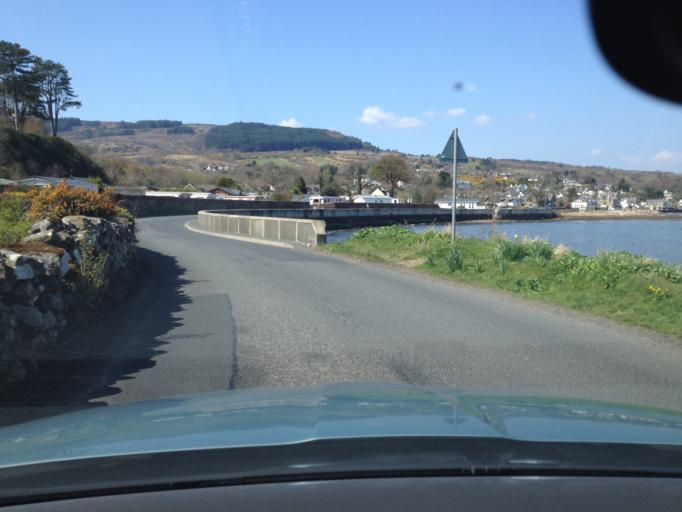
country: GB
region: Scotland
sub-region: North Ayrshire
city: Lamlash
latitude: 55.4800
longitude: -5.0898
